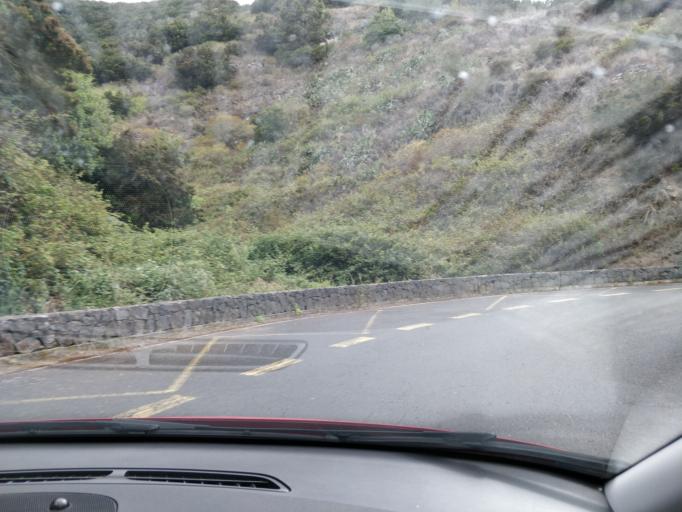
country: ES
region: Canary Islands
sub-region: Provincia de Santa Cruz de Tenerife
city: Santiago del Teide
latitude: 28.3220
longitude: -16.8462
